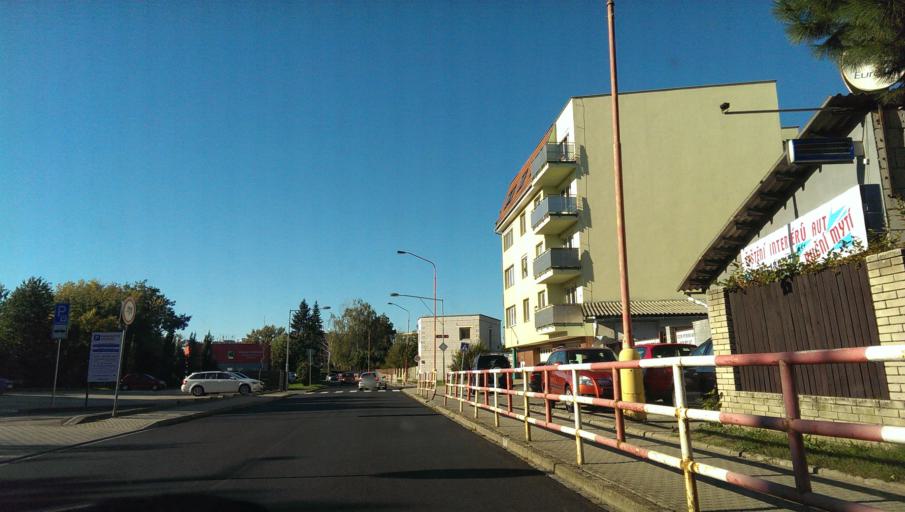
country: CZ
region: Zlin
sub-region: Okres Uherske Hradiste
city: Uherske Hradiste
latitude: 49.0688
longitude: 17.4562
